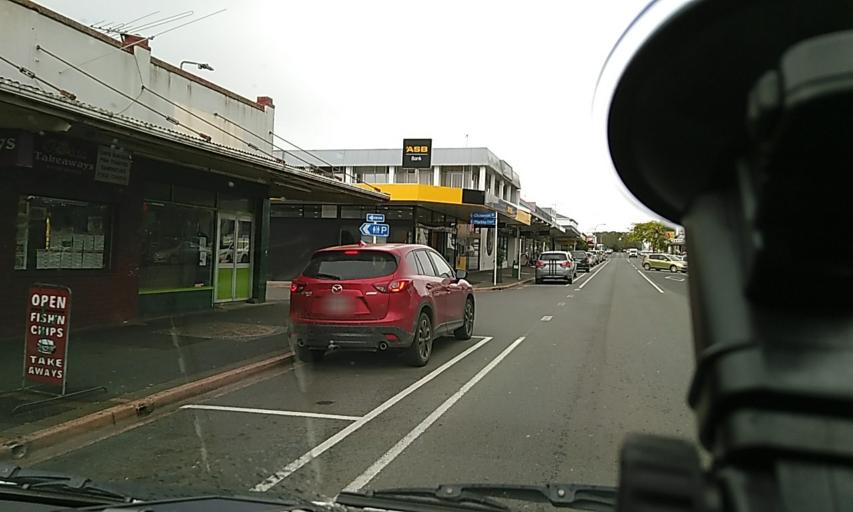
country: NZ
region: Northland
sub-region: Far North District
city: Waimate North
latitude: -35.4078
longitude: 173.7996
